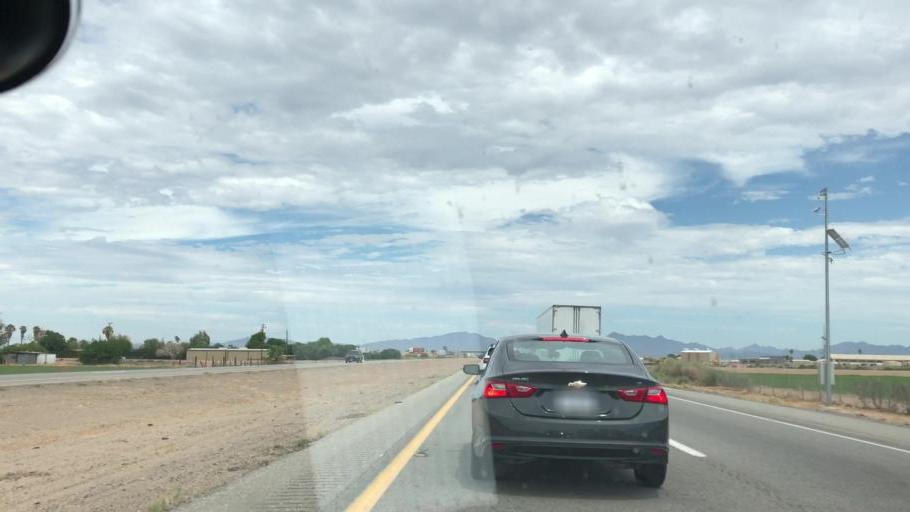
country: US
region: California
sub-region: Riverside County
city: Blythe
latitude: 33.6065
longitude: -114.6517
